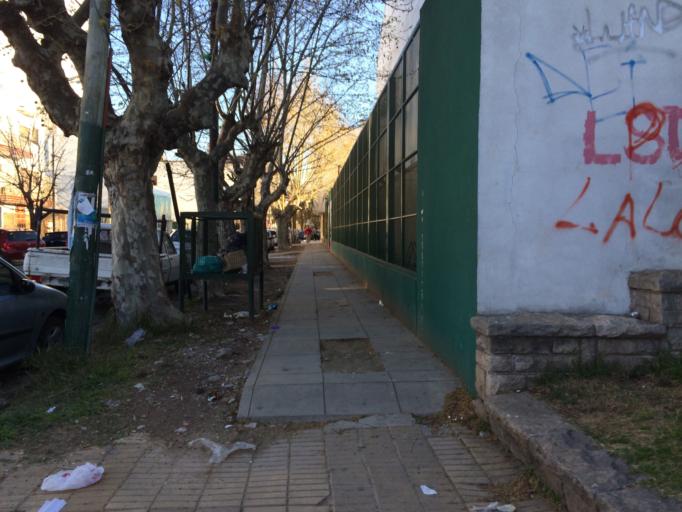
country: AR
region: Buenos Aires
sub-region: Partido de Lomas de Zamora
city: Lomas de Zamora
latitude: -34.7411
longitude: -58.3943
